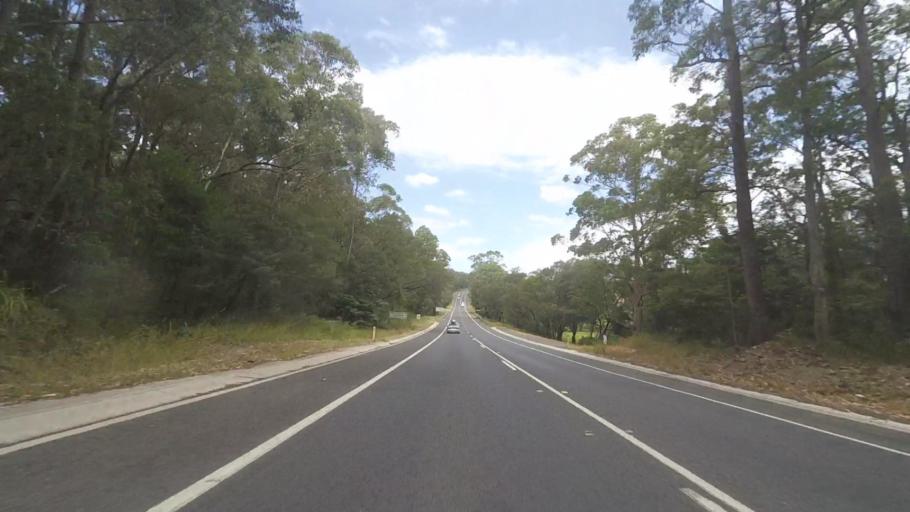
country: AU
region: New South Wales
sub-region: Shoalhaven Shire
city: Milton
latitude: -35.2252
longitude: 150.4357
